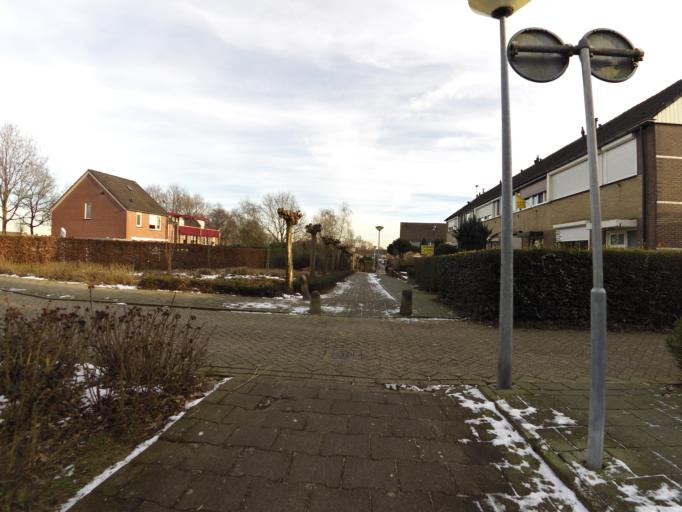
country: NL
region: Gelderland
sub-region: Gemeente Montferland
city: s-Heerenberg
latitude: 51.8821
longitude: 6.2594
